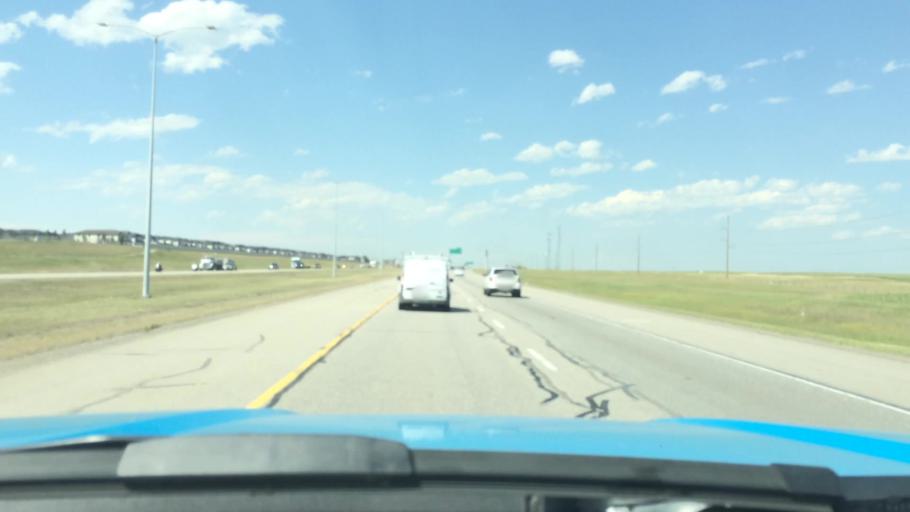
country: CA
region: Alberta
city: Chestermere
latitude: 51.1156
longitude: -113.9208
